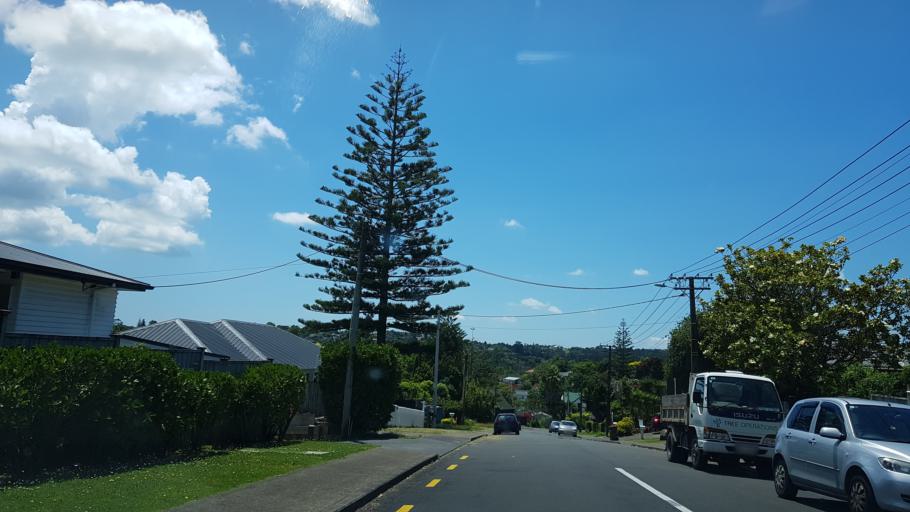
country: NZ
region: Auckland
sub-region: Auckland
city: North Shore
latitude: -36.7975
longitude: 174.7012
